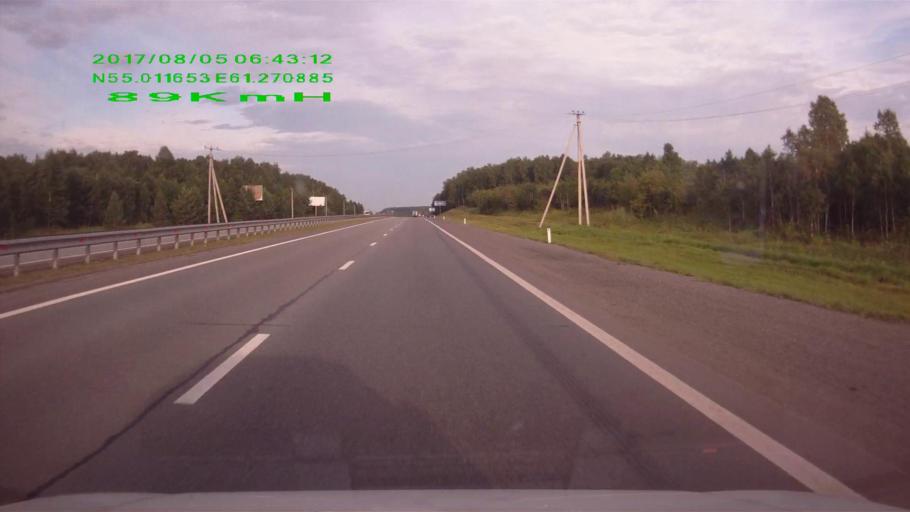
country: RU
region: Chelyabinsk
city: Sargazy
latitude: 55.0116
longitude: 61.2702
